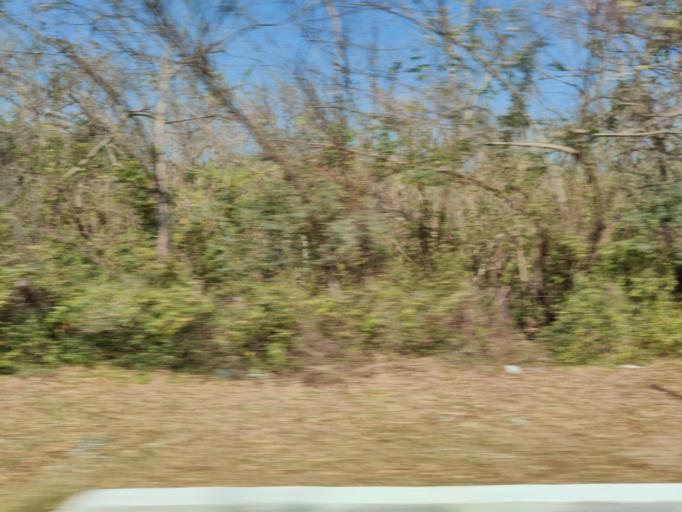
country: CO
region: Atlantico
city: Juan de Acosta
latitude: 10.8476
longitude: -75.1298
